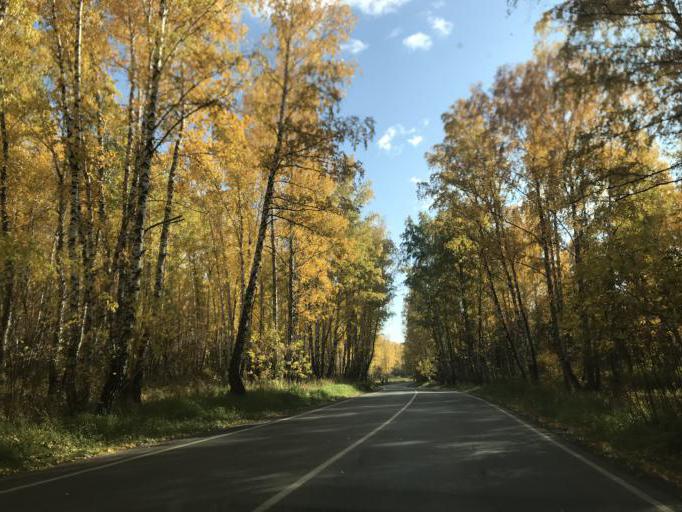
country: RU
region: Chelyabinsk
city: Dolgoderevenskoye
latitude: 55.2728
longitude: 61.3648
